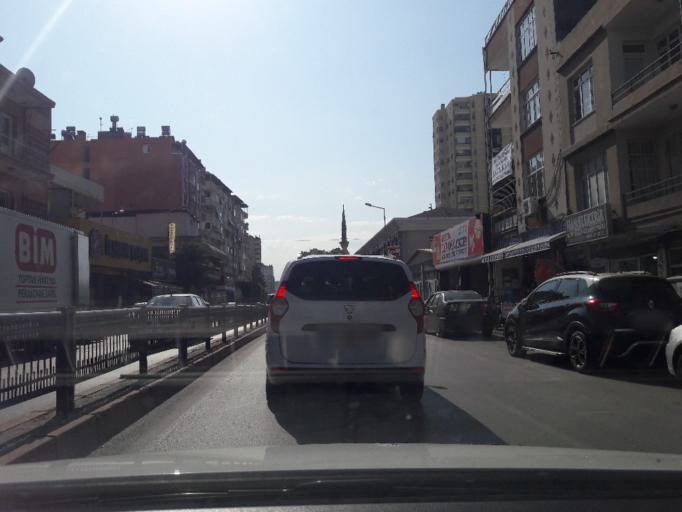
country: TR
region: Adana
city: Adana
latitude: 37.0136
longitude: 35.3225
